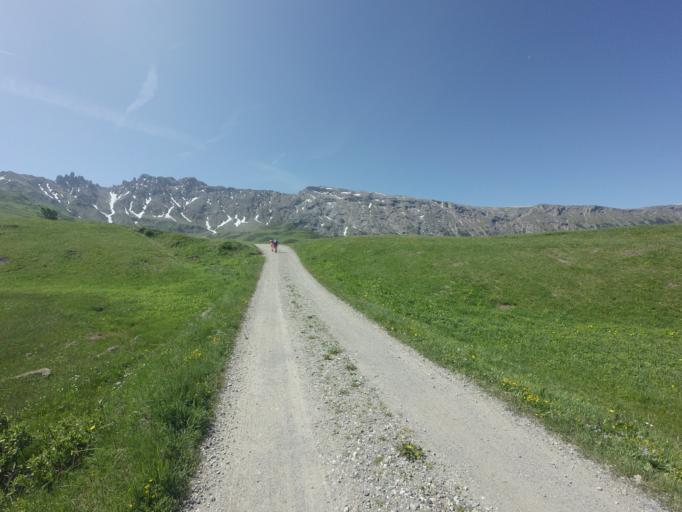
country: IT
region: Trentino-Alto Adige
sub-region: Bolzano
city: Ortisei
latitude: 46.5190
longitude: 11.6257
